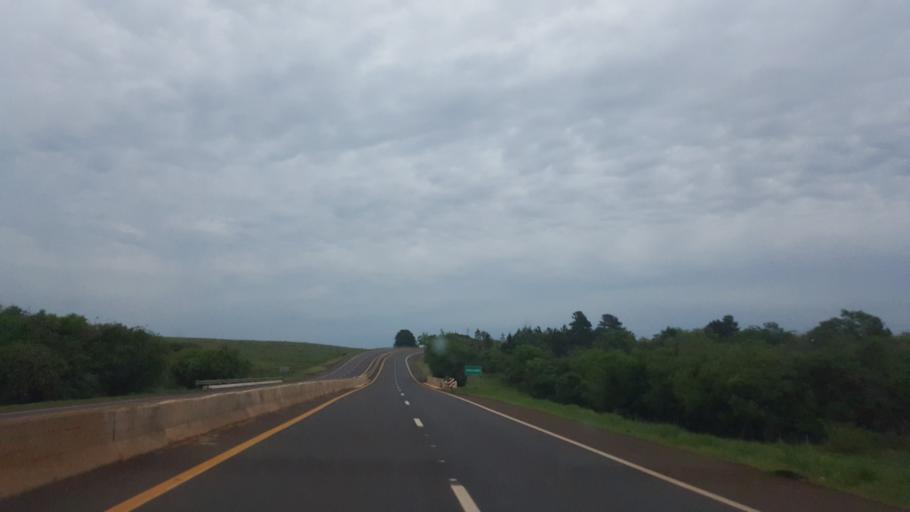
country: AR
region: Misiones
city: Garupa
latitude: -27.5621
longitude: -55.8472
